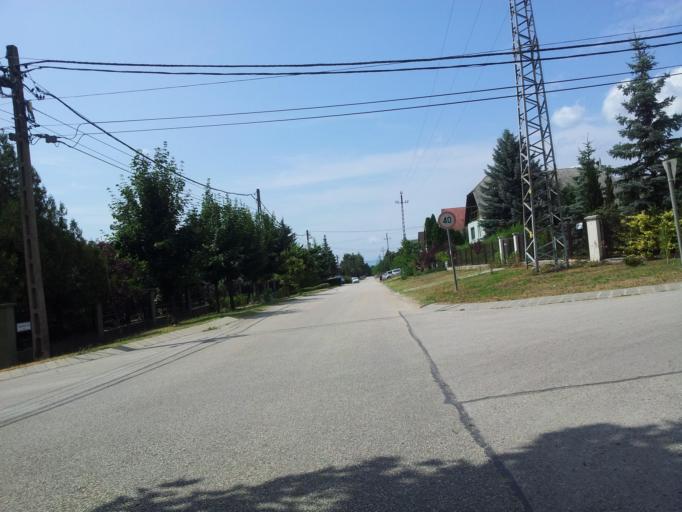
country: HU
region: Pest
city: Veresegyhaz
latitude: 47.6507
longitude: 19.3007
